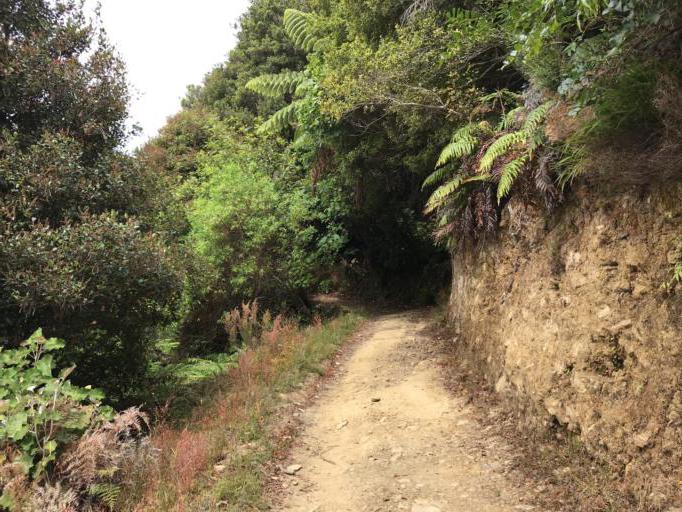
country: NZ
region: Marlborough
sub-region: Marlborough District
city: Picton
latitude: -41.1159
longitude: 174.2043
